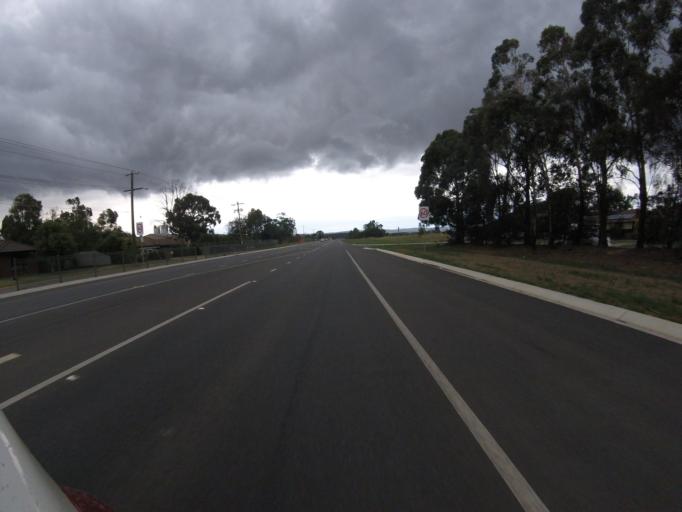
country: AU
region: Victoria
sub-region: Ballarat North
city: Newington
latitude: -37.5241
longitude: 143.8109
